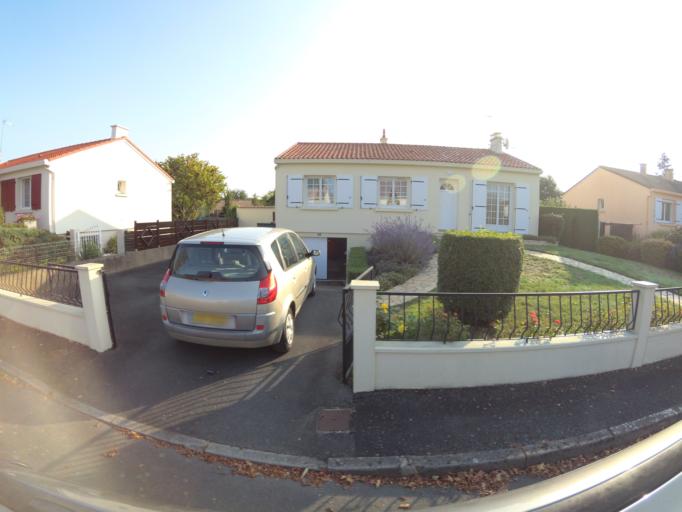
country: FR
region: Pays de la Loire
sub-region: Departement de la Vendee
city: Saint-Hilaire-de-Loulay
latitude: 47.0071
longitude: -1.3333
